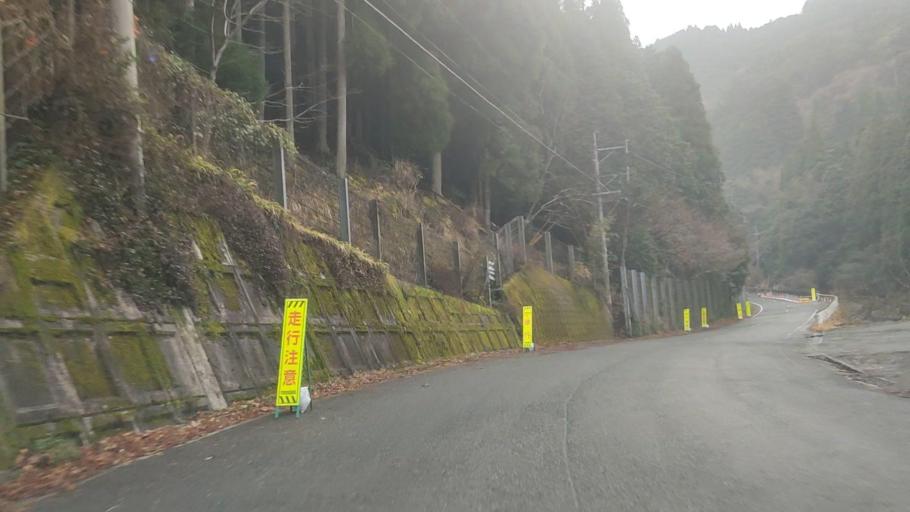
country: JP
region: Kumamoto
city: Matsubase
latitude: 32.6039
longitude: 130.8870
